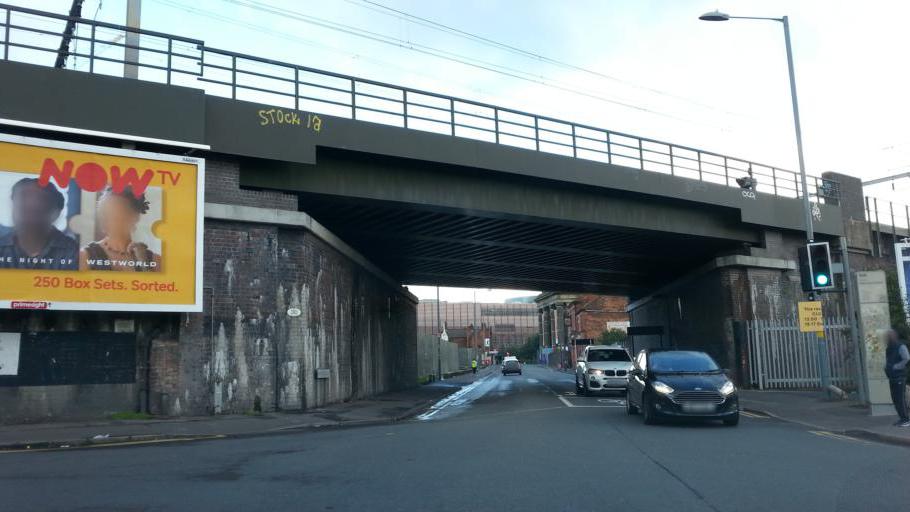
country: GB
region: England
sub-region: City and Borough of Birmingham
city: Birmingham
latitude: 52.4799
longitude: -1.8875
